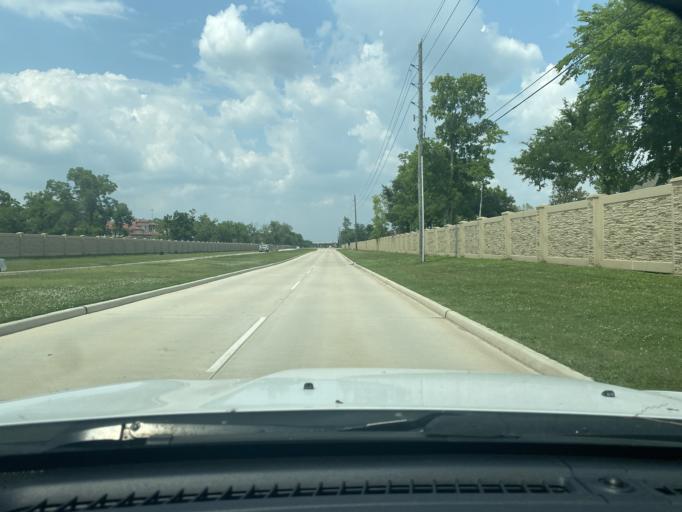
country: US
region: Texas
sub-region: Fort Bend County
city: Greatwood
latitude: 29.5481
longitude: -95.7209
